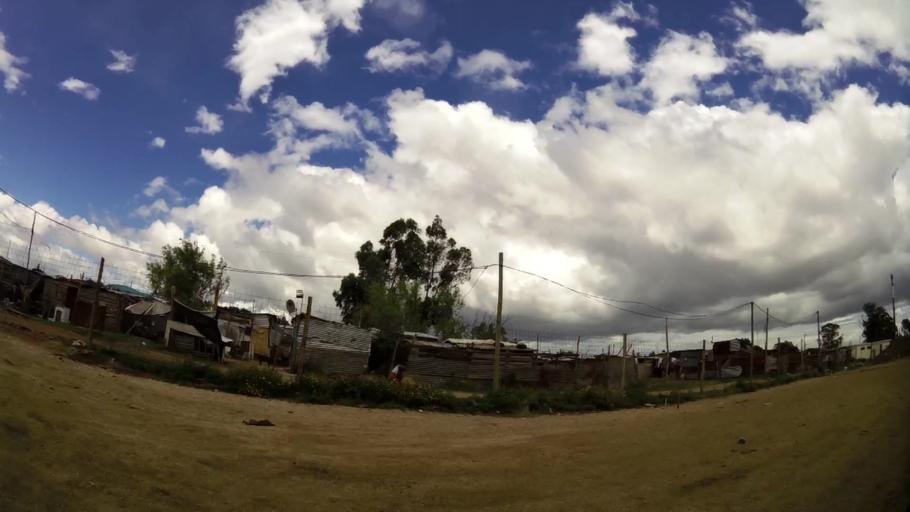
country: UY
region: Montevideo
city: Montevideo
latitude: -34.8223
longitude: -56.1639
